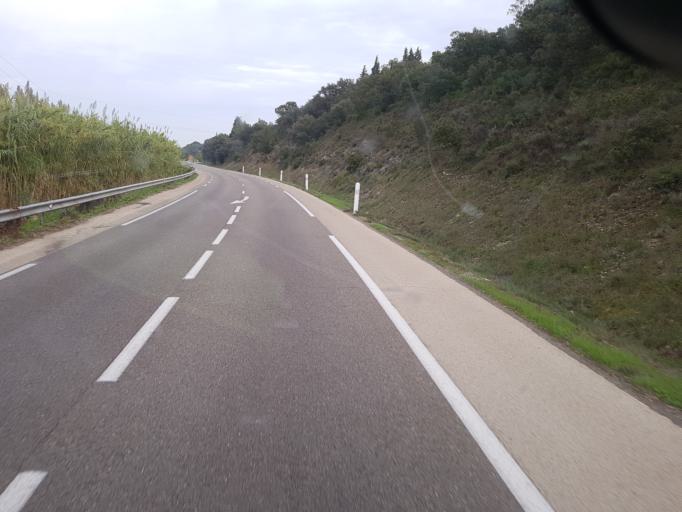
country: FR
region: Languedoc-Roussillon
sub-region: Departement du Gard
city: Aramon
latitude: 43.8957
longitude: 4.7100
